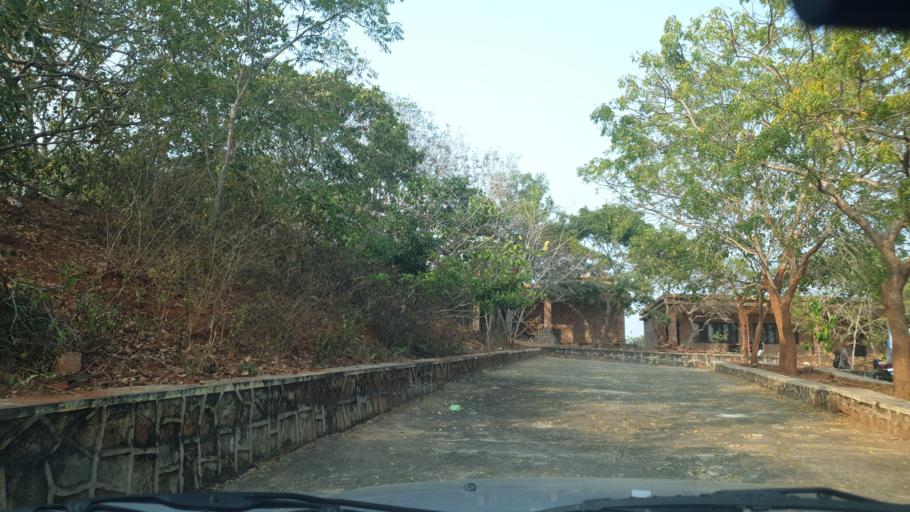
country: IN
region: Andhra Pradesh
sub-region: Srikakulam
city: Narasannapeta
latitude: 18.3332
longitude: 84.0460
